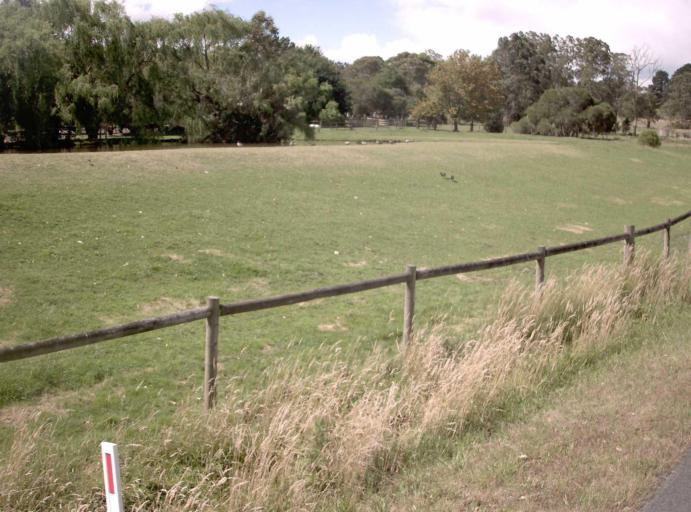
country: AU
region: Victoria
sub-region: Latrobe
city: Morwell
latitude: -38.1623
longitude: 146.4052
